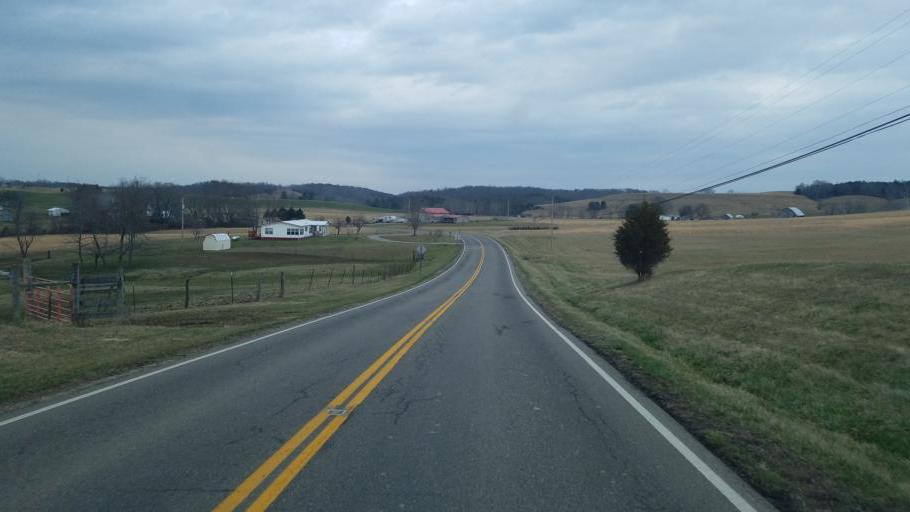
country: US
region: Ohio
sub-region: Jackson County
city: Oak Hill
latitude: 38.8239
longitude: -82.3987
